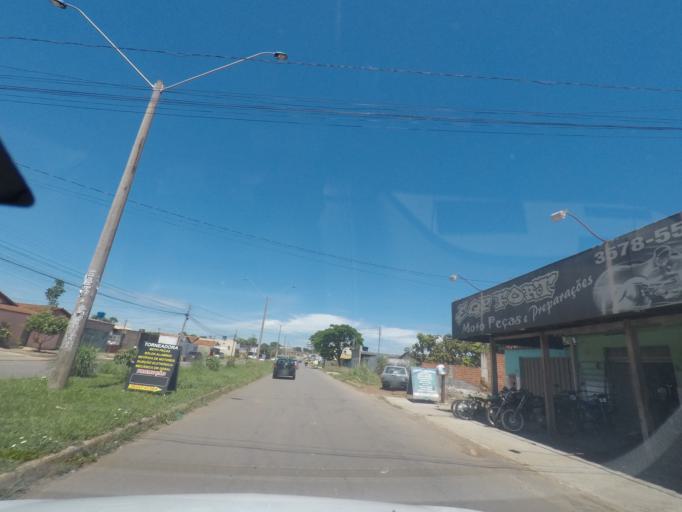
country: BR
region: Goias
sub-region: Aparecida De Goiania
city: Aparecida de Goiania
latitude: -16.7706
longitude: -49.3281
